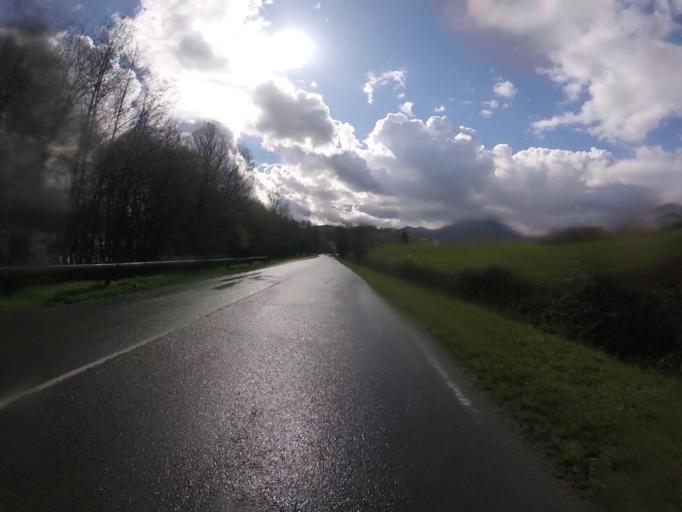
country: FR
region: Aquitaine
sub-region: Departement des Pyrenees-Atlantiques
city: Sare
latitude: 43.3125
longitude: -1.5742
